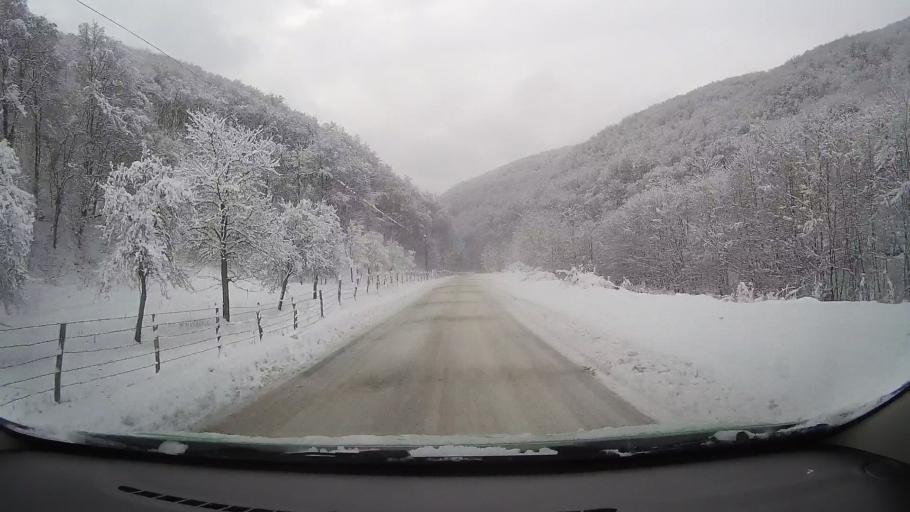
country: RO
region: Alba
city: Pianu de Sus
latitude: 45.8749
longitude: 23.4925
